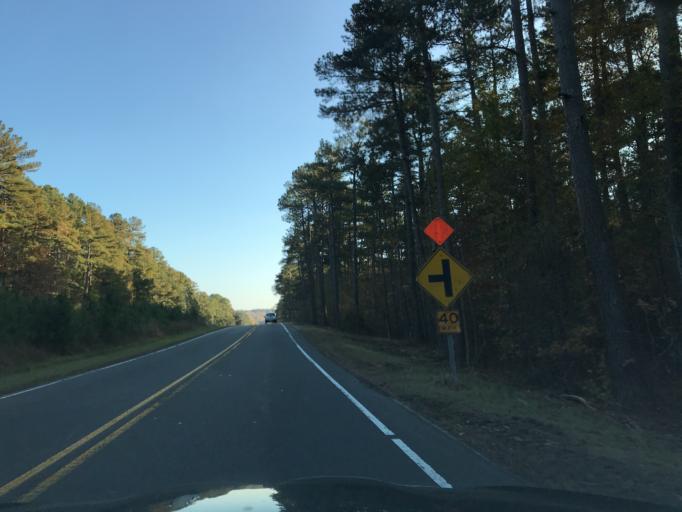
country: US
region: North Carolina
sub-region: Granville County
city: Creedmoor
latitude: 36.0250
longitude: -78.6963
